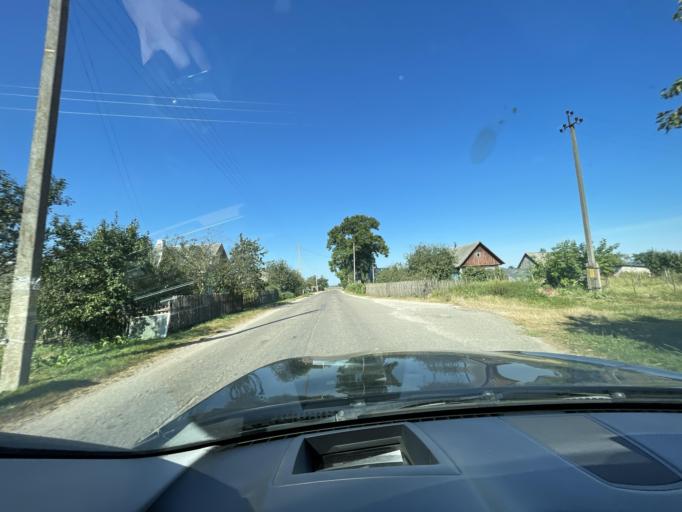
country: BY
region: Grodnenskaya
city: Hrodna
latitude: 53.7179
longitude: 23.9859
